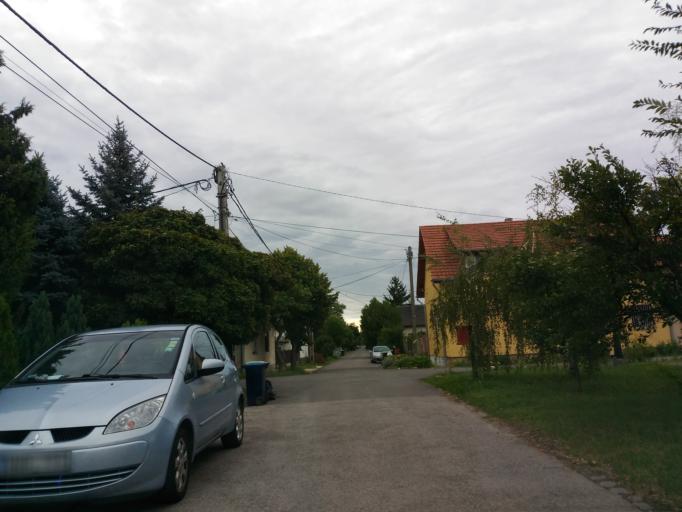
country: HU
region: Pest
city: Diosd
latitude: 47.3950
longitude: 18.9758
